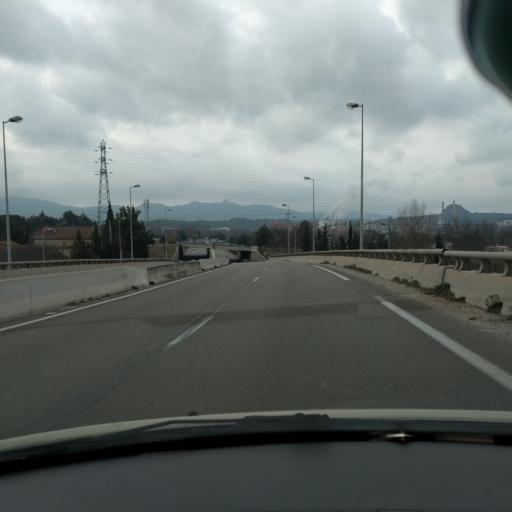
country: FR
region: Provence-Alpes-Cote d'Azur
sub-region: Departement des Bouches-du-Rhone
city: Gardanne
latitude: 43.4648
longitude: 5.4659
